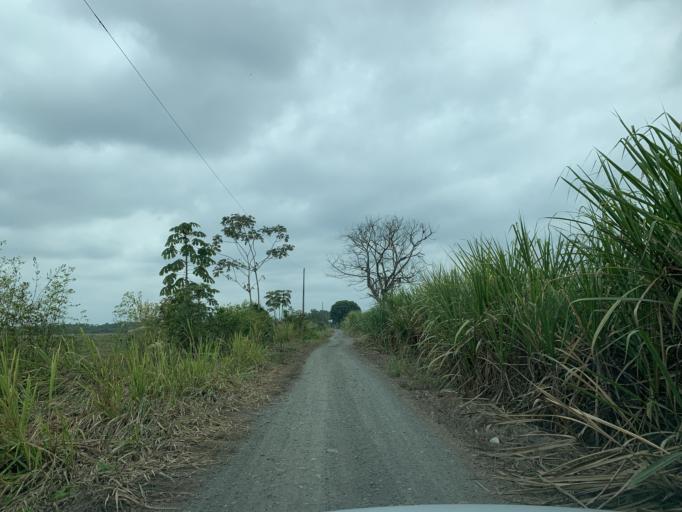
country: EC
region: Canar
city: La Troncal
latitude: -2.3506
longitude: -79.4607
